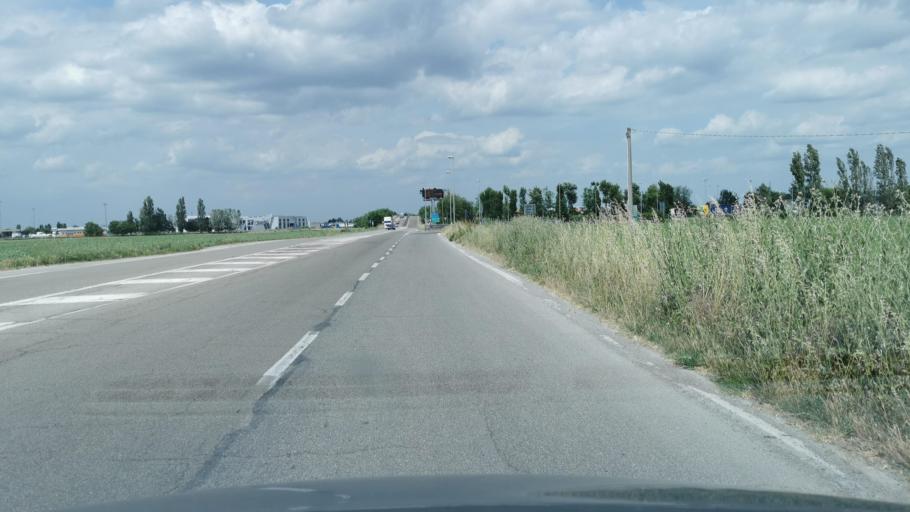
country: IT
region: Emilia-Romagna
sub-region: Provincia di Bologna
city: Castel San Pietro Terme
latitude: 44.4227
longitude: 11.6015
